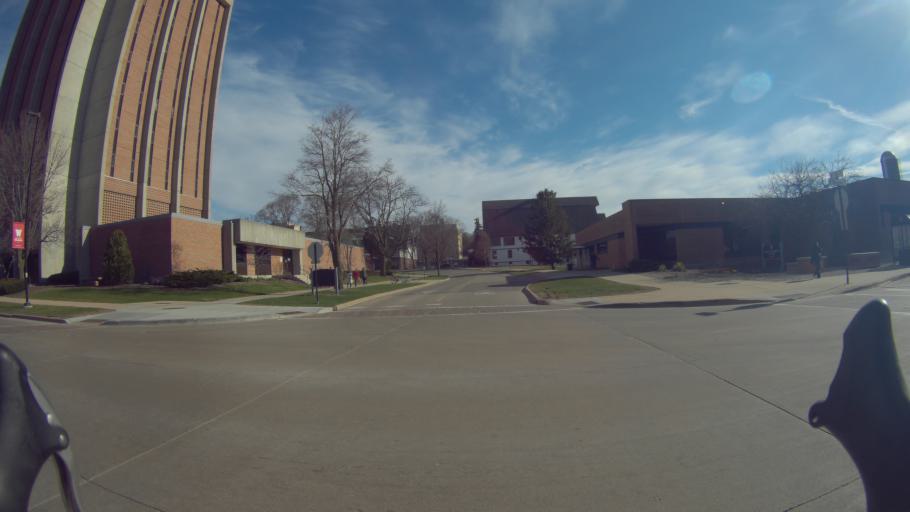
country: US
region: Wisconsin
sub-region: Dane County
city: Madison
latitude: 43.0767
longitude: -89.4159
